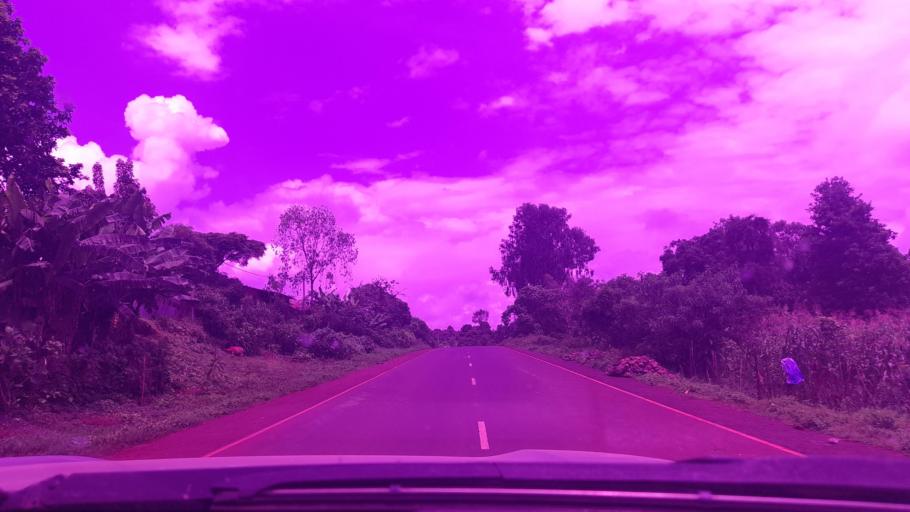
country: ET
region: Oromiya
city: Metu
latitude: 8.3353
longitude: 35.7269
